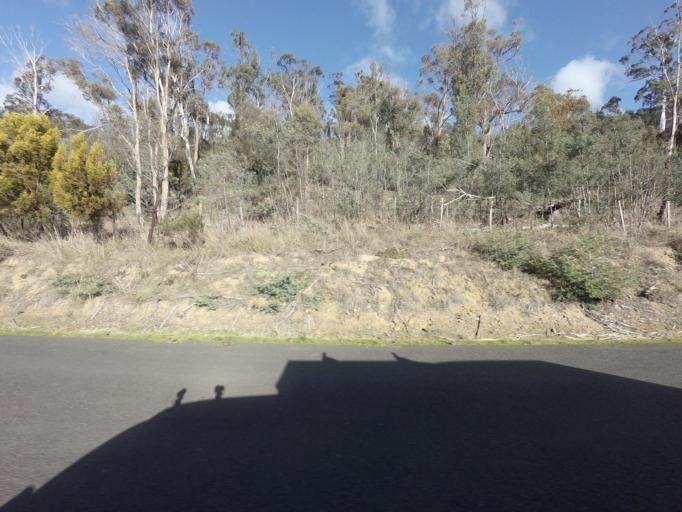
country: AU
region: Tasmania
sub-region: Derwent Valley
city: New Norfolk
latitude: -42.8034
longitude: 147.1489
